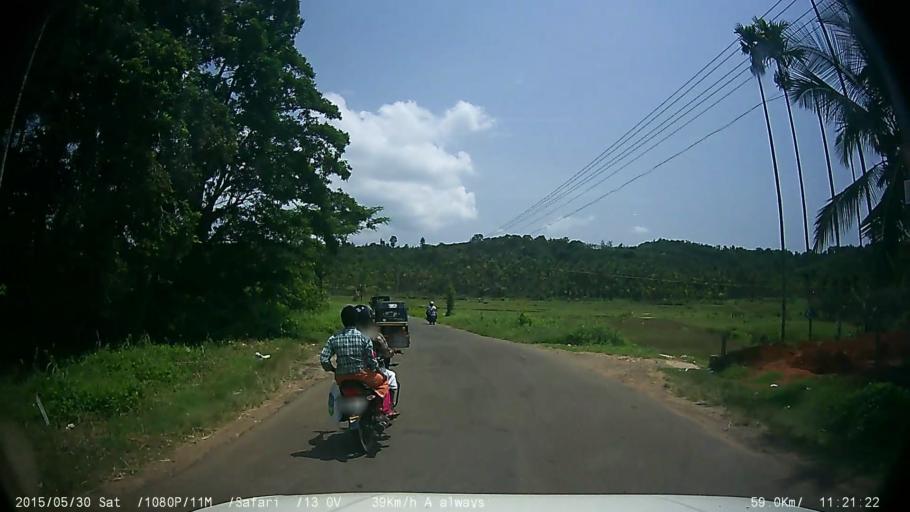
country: IN
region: Kerala
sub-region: Wayanad
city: Panamaram
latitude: 11.8011
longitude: 76.0370
